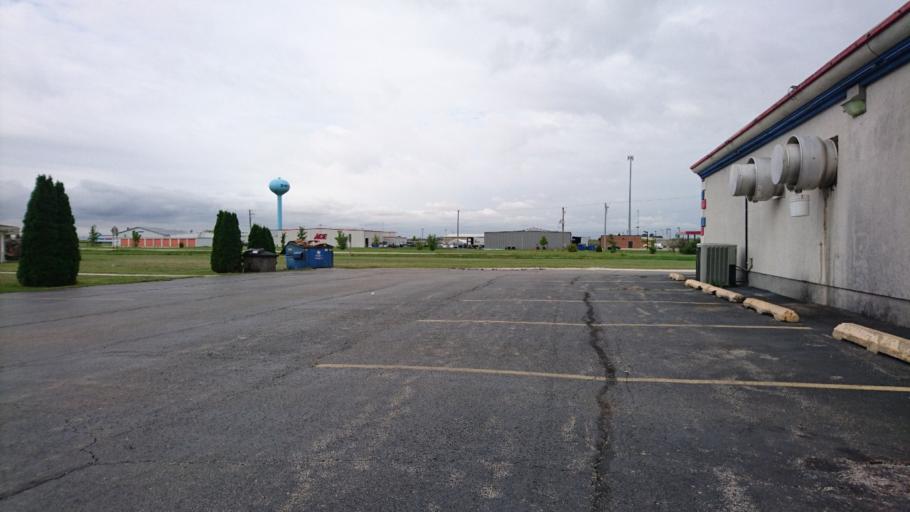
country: US
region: Illinois
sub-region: Livingston County
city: Dwight
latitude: 41.0931
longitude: -88.4400
